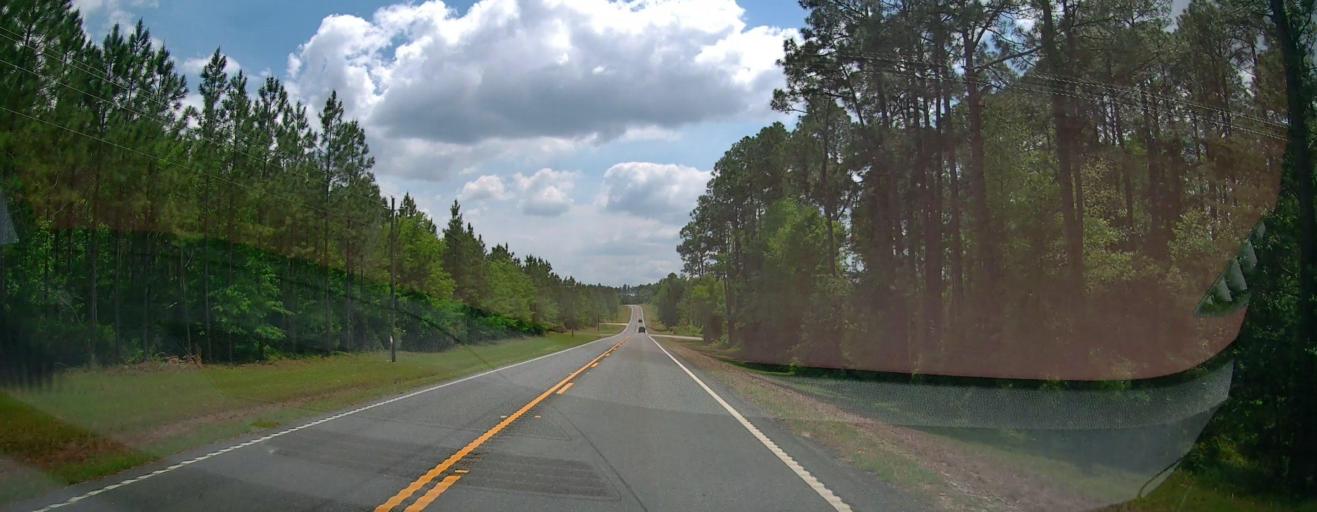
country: US
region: Georgia
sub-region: Treutlen County
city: Soperton
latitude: 32.4199
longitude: -82.6083
